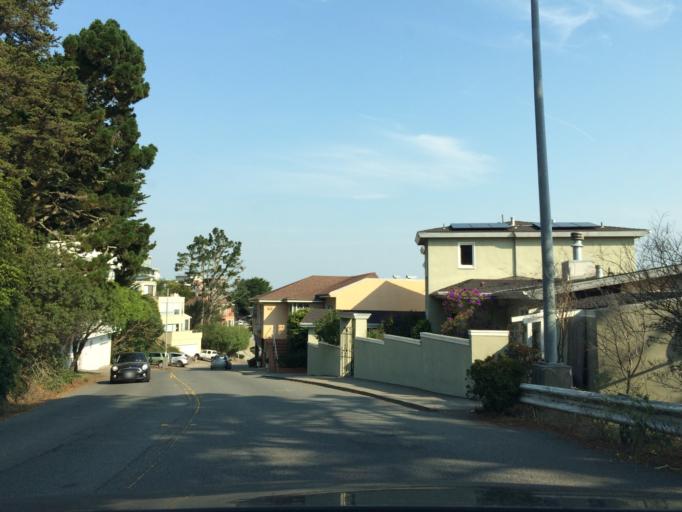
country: US
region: California
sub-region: San Francisco County
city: San Francisco
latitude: 37.7569
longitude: -122.4471
